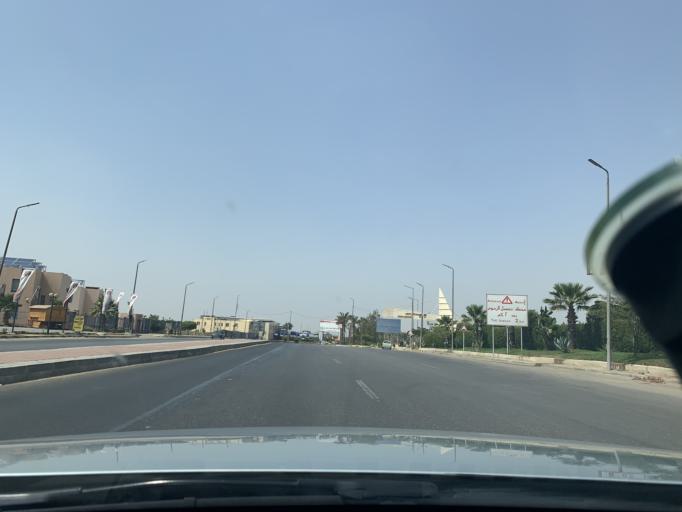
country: EG
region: Muhafazat al Qalyubiyah
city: Al Khankah
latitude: 30.0940
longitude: 31.3827
